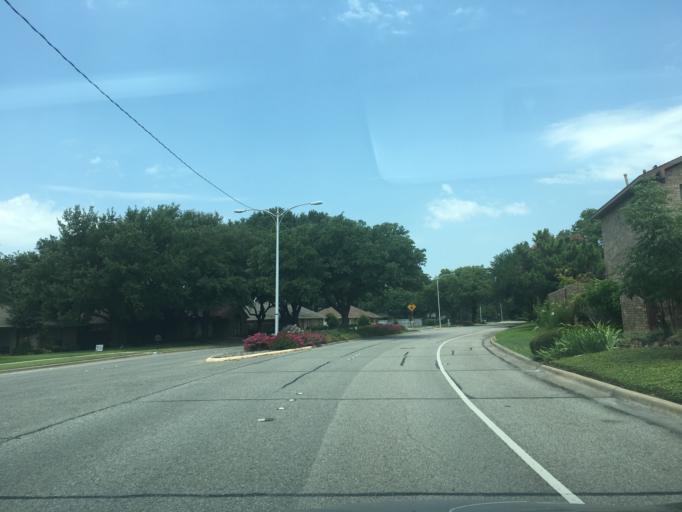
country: US
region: Texas
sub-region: Dallas County
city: Farmers Branch
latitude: 32.9323
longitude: -96.8657
